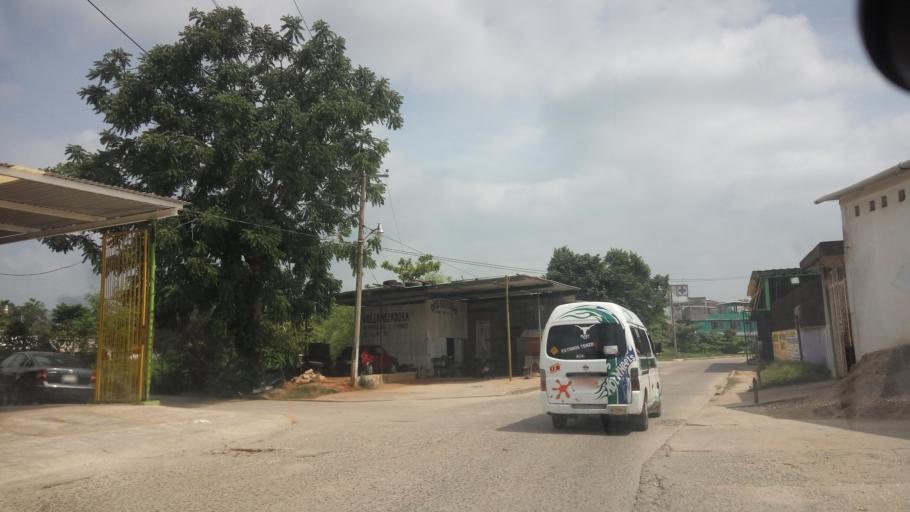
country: MX
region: Chiapas
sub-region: Reforma
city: El Carmen (El Limon)
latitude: 17.8691
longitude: -93.1493
